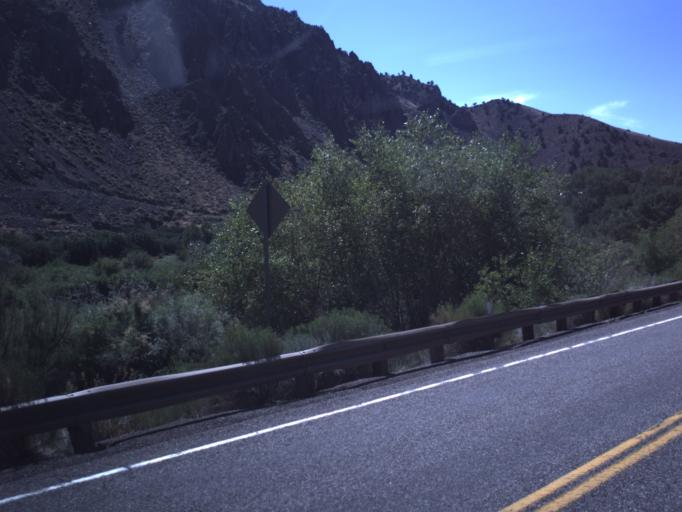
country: US
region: Utah
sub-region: Sevier County
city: Monroe
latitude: 38.5068
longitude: -112.2593
